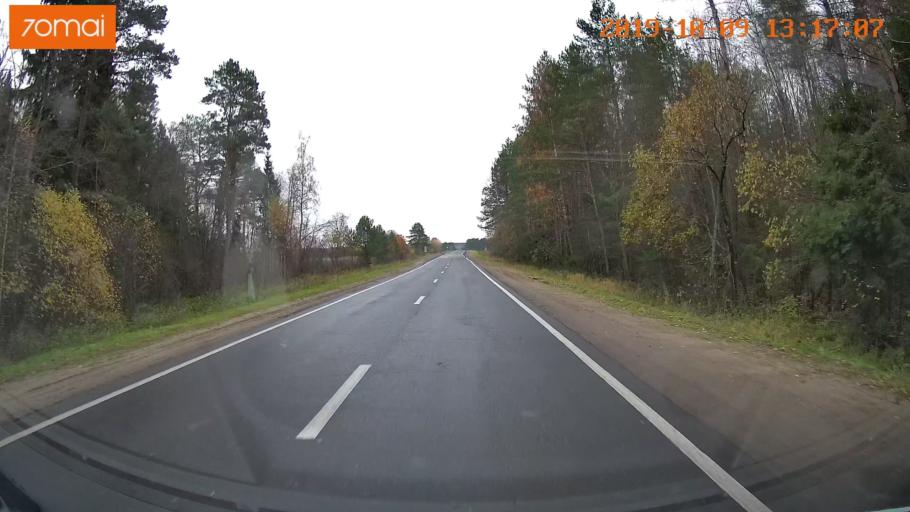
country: RU
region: Jaroslavl
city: Lyubim
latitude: 58.3563
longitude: 40.7756
